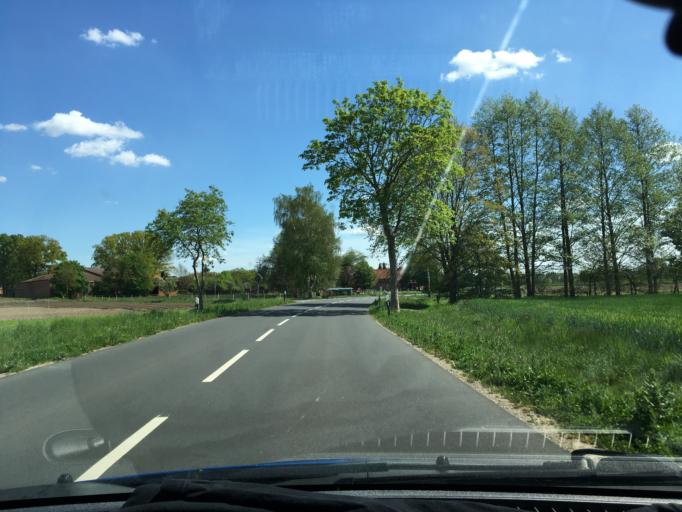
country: DE
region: Lower Saxony
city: Stoetze
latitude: 53.0731
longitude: 10.7687
